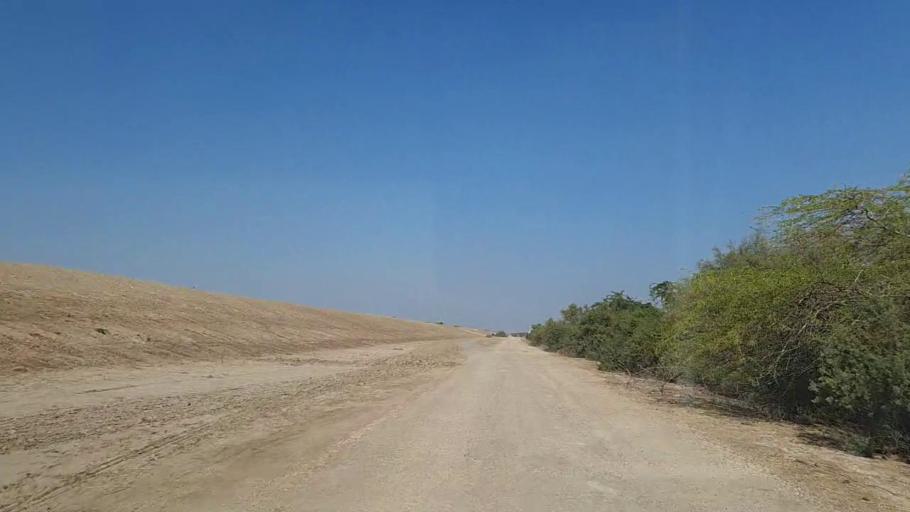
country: PK
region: Sindh
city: Chuhar Jamali
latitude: 24.4629
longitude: 68.0035
